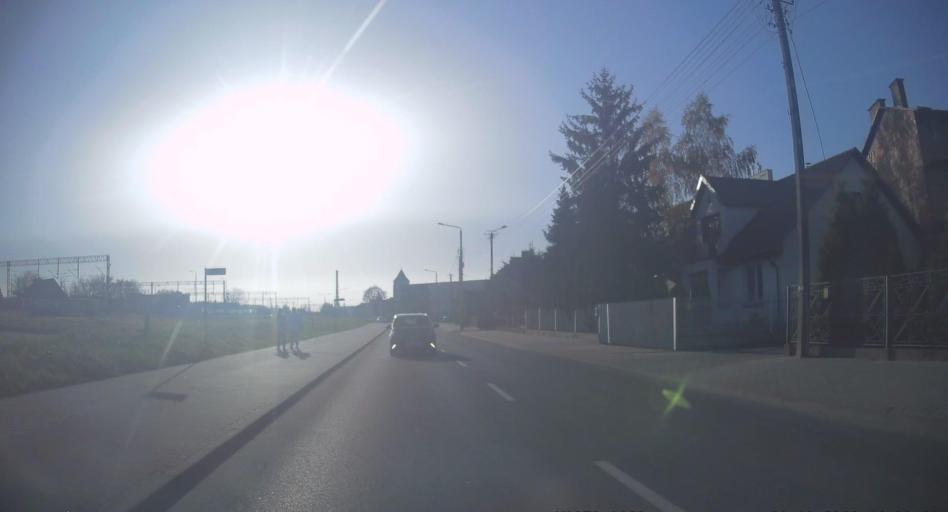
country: PL
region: Subcarpathian Voivodeship
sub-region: Powiat debicki
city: Debica
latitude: 50.0546
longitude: 21.4035
